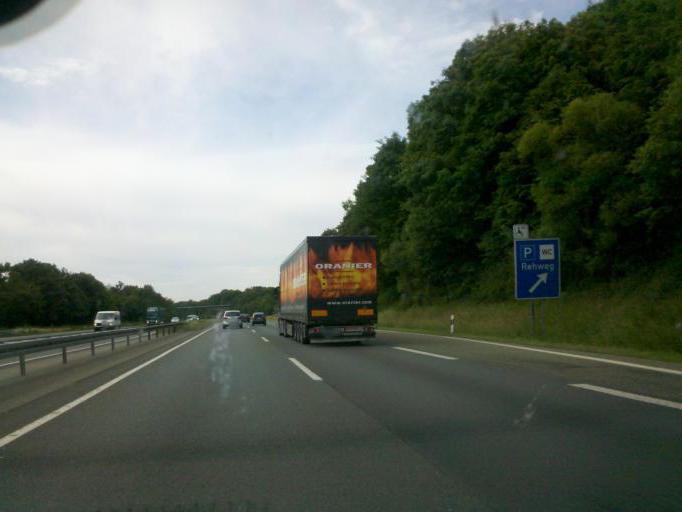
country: DE
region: North Rhine-Westphalia
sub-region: Regierungsbezirk Arnsberg
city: Nachrodt-Wiblingwerde
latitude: 51.2677
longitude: 7.6017
